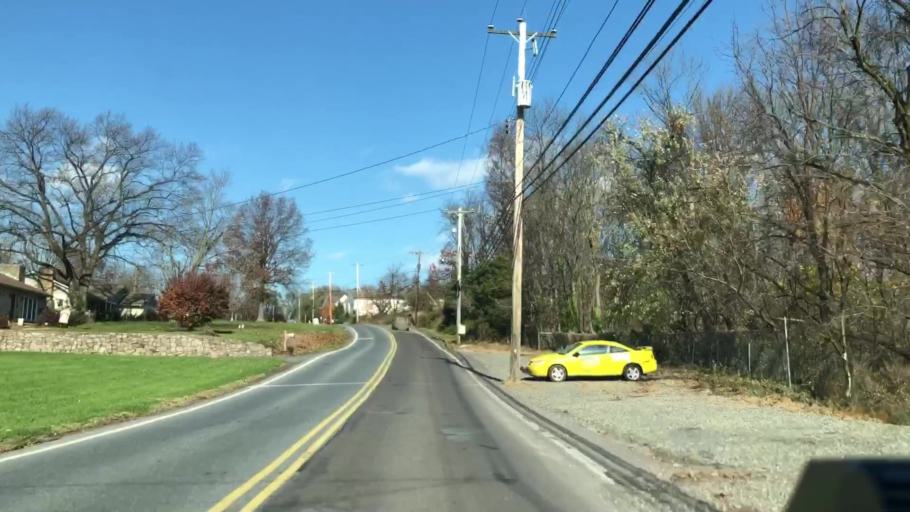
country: US
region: Pennsylvania
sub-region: Montgomery County
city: Halfway House
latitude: 40.2642
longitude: -75.6420
